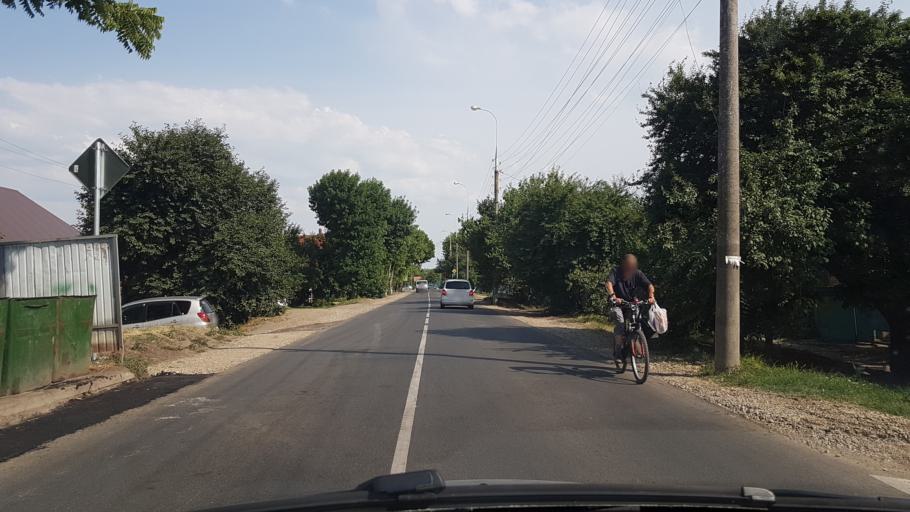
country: RU
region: Krasnodarskiy
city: Pashkovskiy
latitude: 45.0284
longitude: 39.1243
